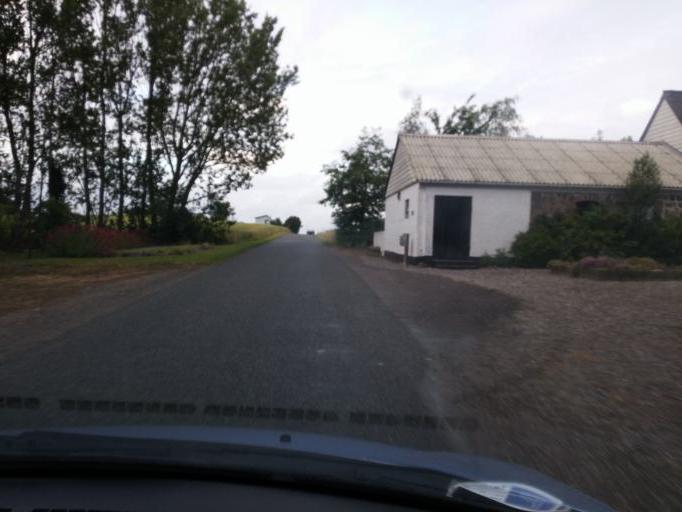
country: DK
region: South Denmark
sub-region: Kerteminde Kommune
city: Munkebo
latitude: 55.5195
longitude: 10.5757
